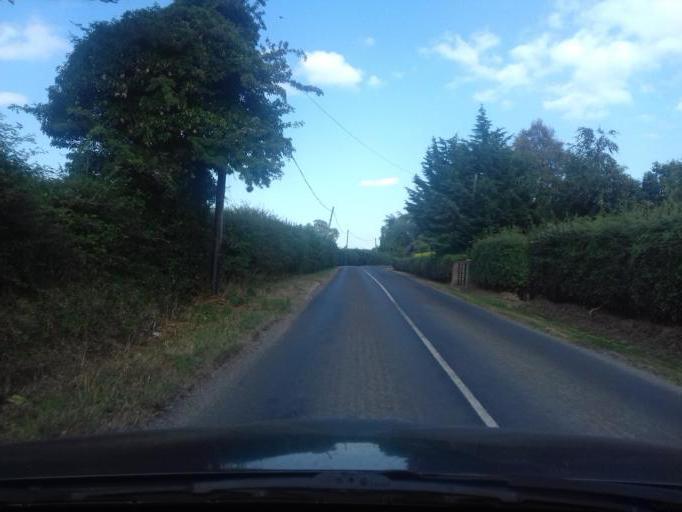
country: IE
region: Leinster
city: Hartstown
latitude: 53.4448
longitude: -6.4249
